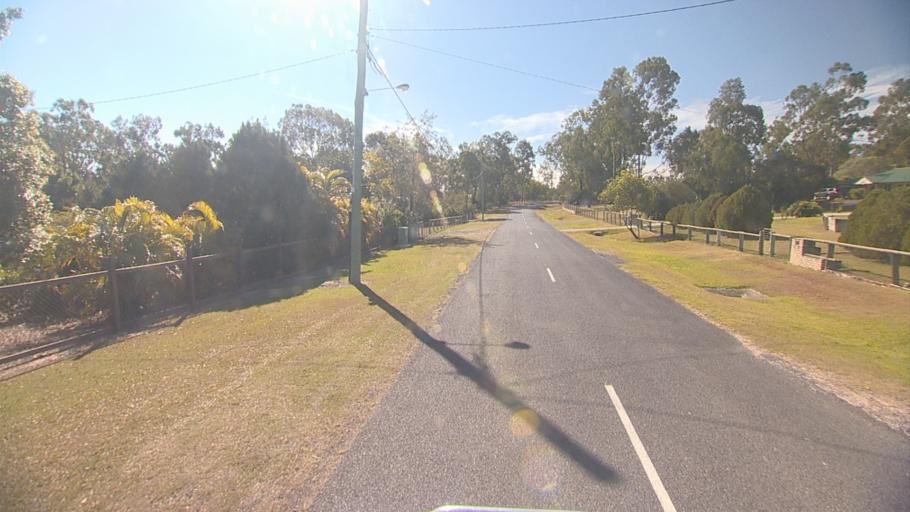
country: AU
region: Queensland
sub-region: Logan
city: North Maclean
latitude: -27.7324
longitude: 152.9609
